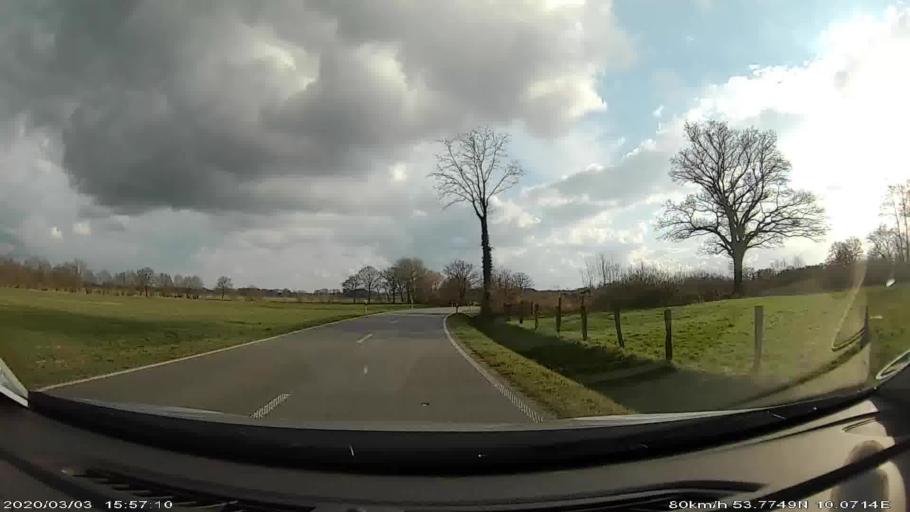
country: DE
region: Schleswig-Holstein
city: Tangstedt
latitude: 53.7764
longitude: 10.0708
